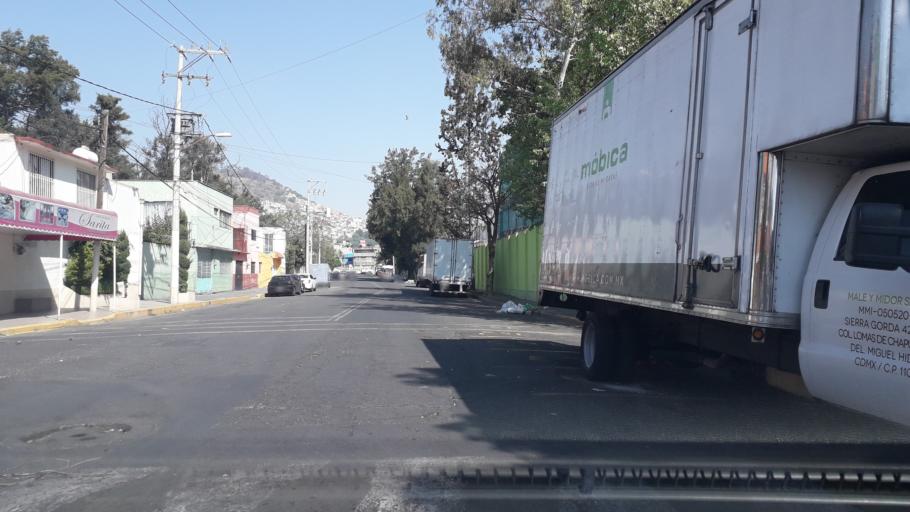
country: MX
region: Mexico City
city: Gustavo A. Madero
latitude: 19.5043
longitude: -99.0968
